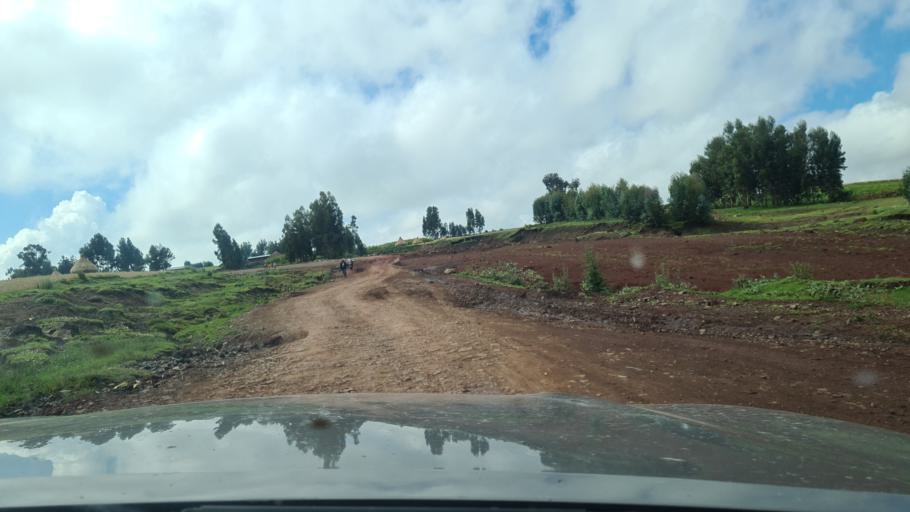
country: ET
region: Oromiya
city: Huruta
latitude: 8.1260
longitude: 39.4361
